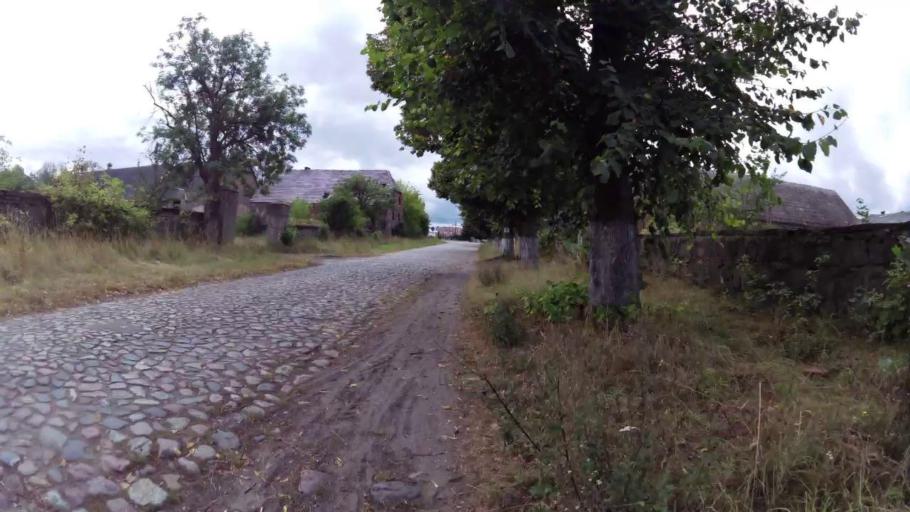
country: PL
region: West Pomeranian Voivodeship
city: Trzcinsko Zdroj
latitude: 52.8825
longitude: 14.7114
